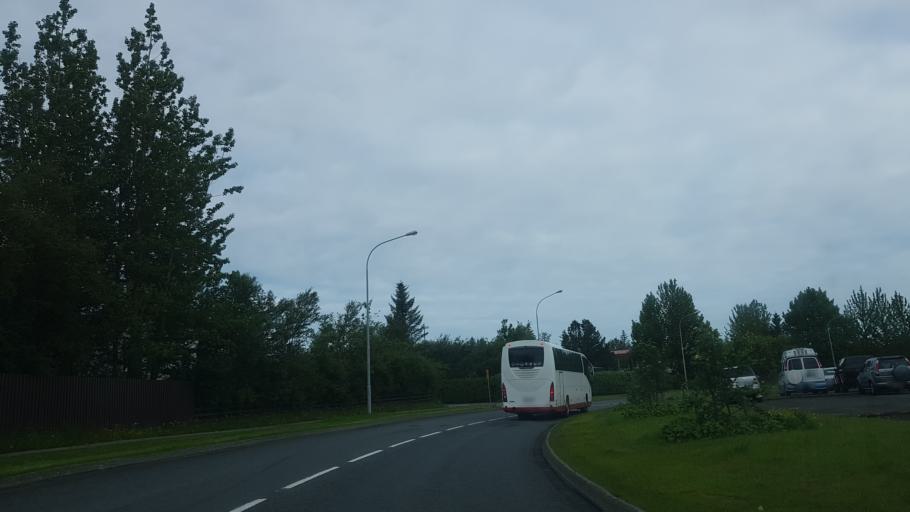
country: IS
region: Capital Region
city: Reykjavik
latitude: 64.0996
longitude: -21.8565
